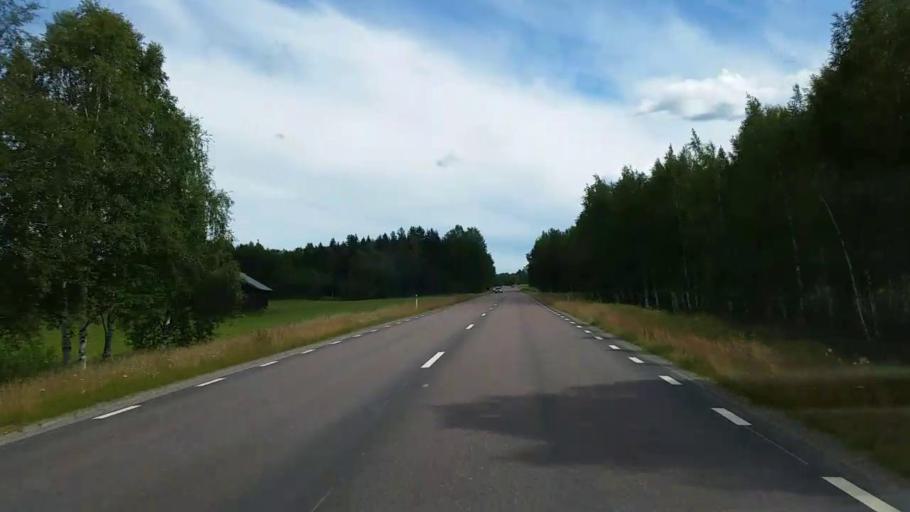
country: SE
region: Gaevleborg
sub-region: Ovanakers Kommun
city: Edsbyn
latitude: 61.3690
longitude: 15.8620
